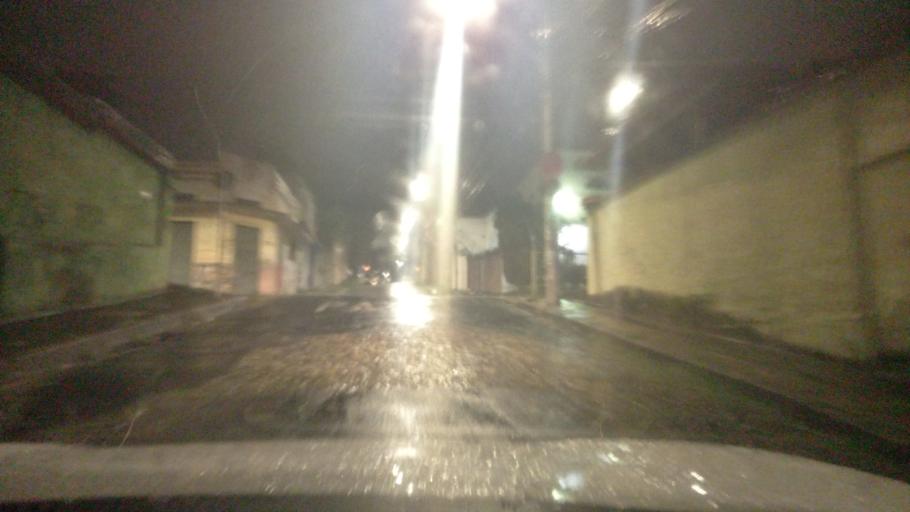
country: BR
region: Minas Gerais
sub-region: Belo Horizonte
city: Belo Horizonte
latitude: -19.9130
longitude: -43.9697
